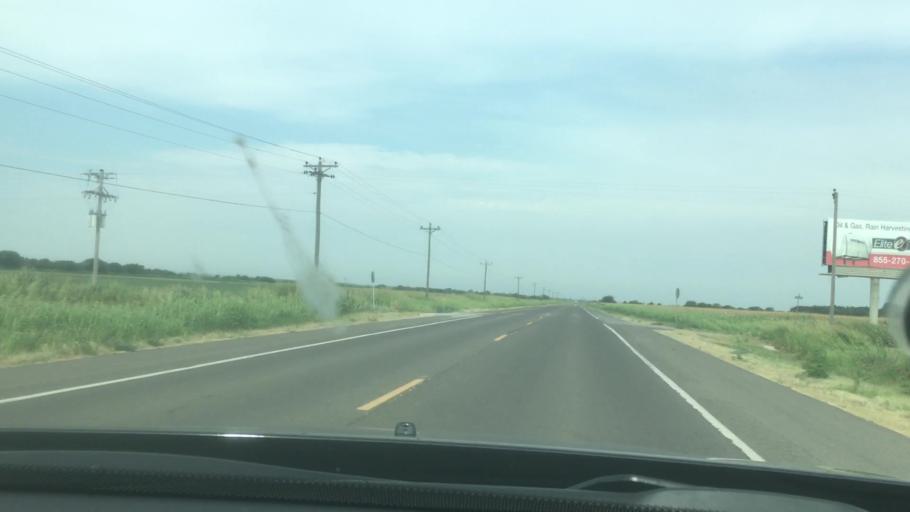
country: US
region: Oklahoma
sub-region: Garvin County
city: Maysville
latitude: 34.8192
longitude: -97.4746
